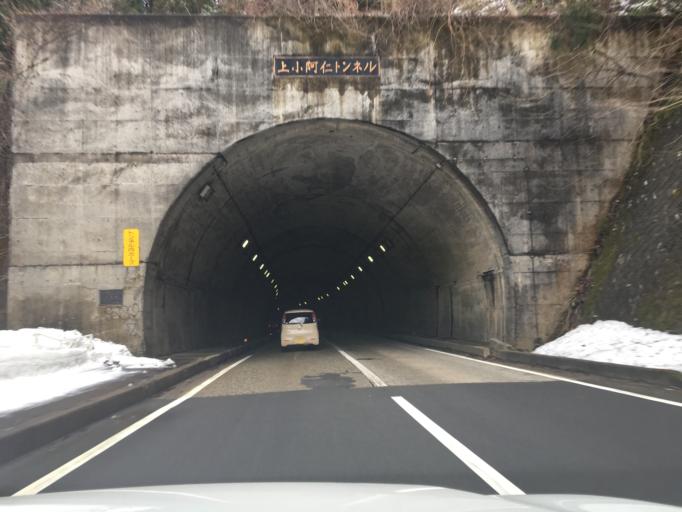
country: JP
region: Akita
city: Takanosu
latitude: 39.9957
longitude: 140.2558
